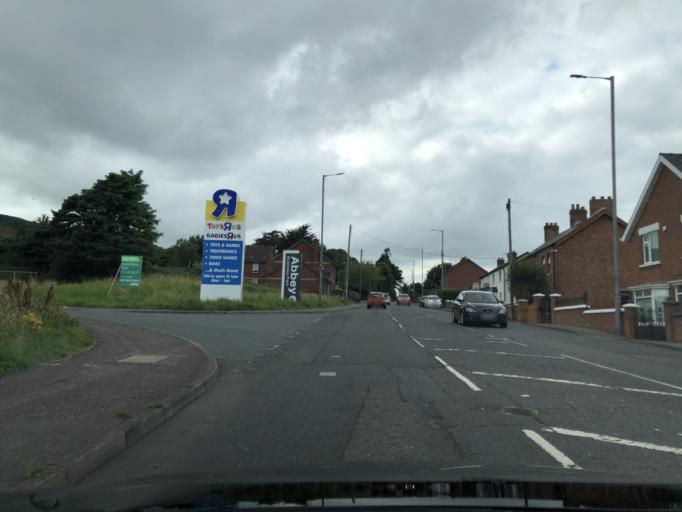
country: GB
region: Northern Ireland
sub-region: Newtownabbey District
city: Newtownabbey
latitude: 54.6531
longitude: -5.9206
